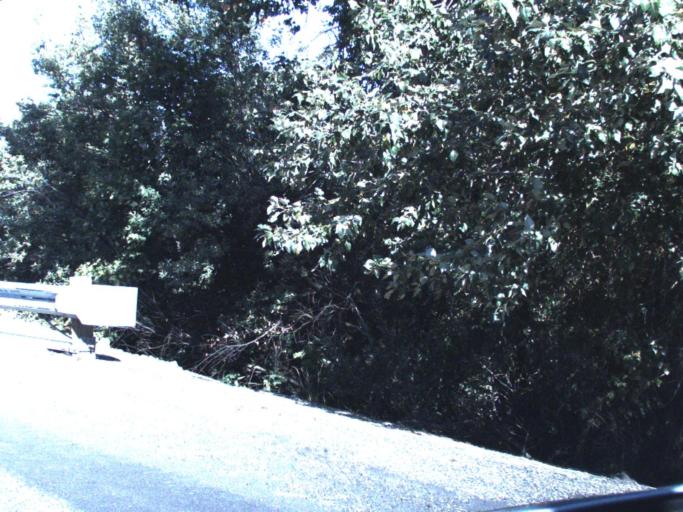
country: US
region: Washington
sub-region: Walla Walla County
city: Waitsburg
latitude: 46.2738
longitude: -118.2210
